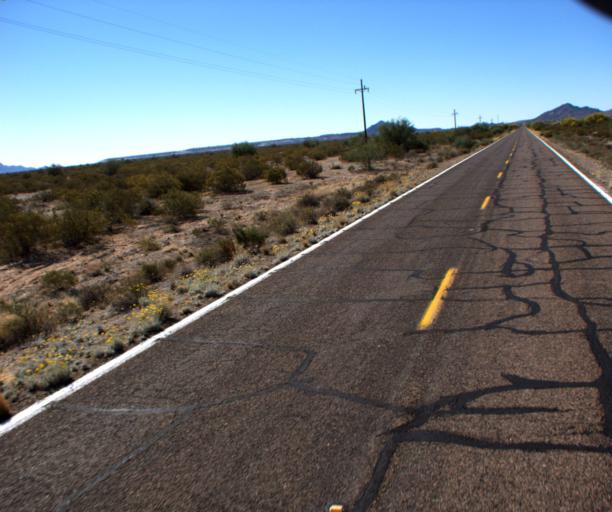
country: US
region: Arizona
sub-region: Pima County
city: Ajo
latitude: 32.4412
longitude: -112.8711
